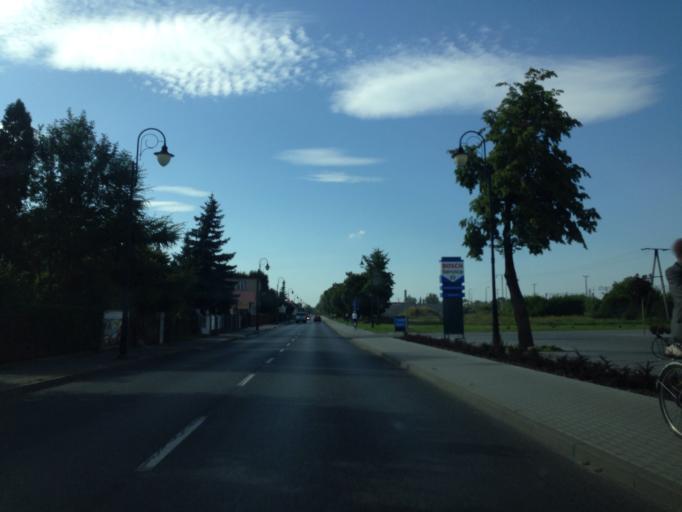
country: PL
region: Kujawsko-Pomorskie
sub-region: Powiat aleksandrowski
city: Aleksandrow Kujawski
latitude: 52.8667
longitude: 18.7060
